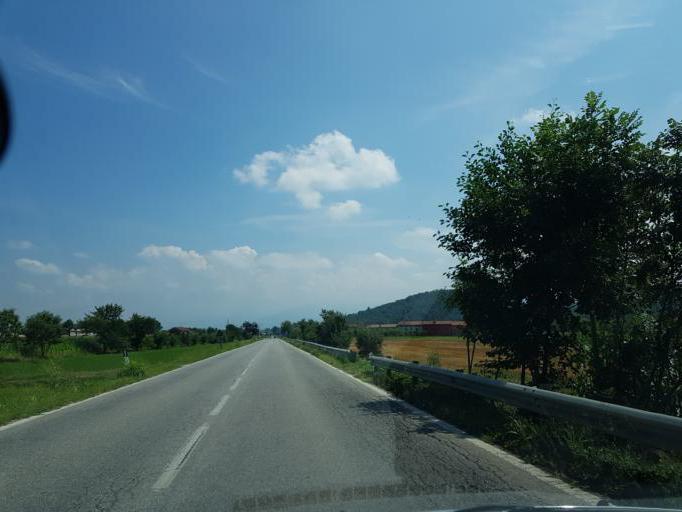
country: IT
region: Piedmont
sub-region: Provincia di Cuneo
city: Caraglio
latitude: 44.4413
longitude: 7.4100
